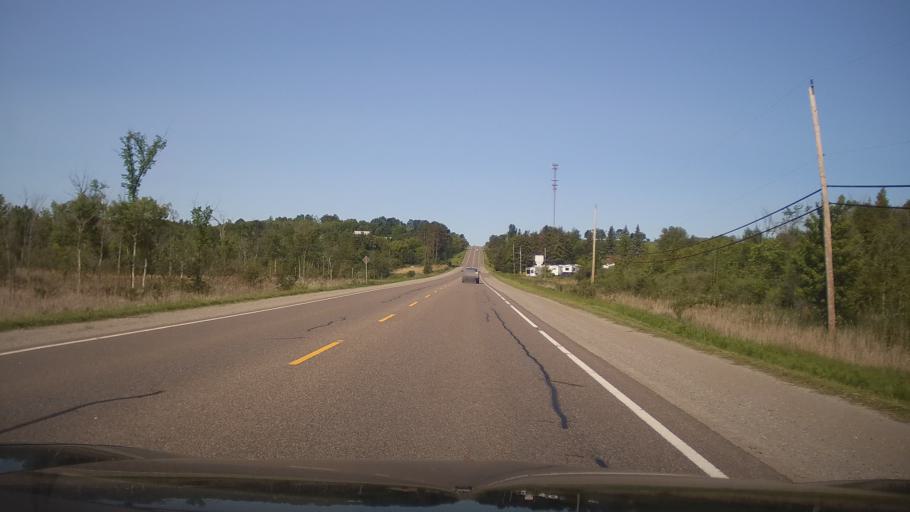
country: CA
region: Ontario
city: Omemee
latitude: 44.3189
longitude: -78.4781
